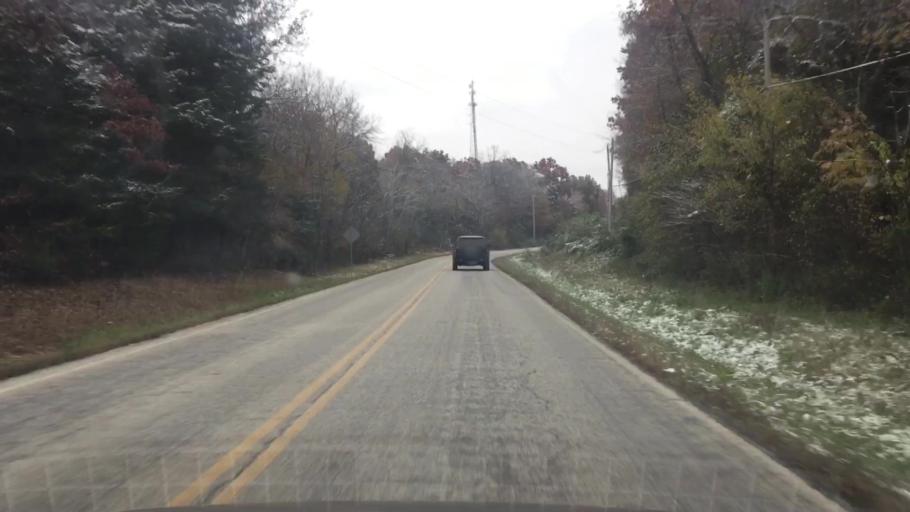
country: US
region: Missouri
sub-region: Saint Clair County
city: Osceola
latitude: 38.0432
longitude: -93.6911
